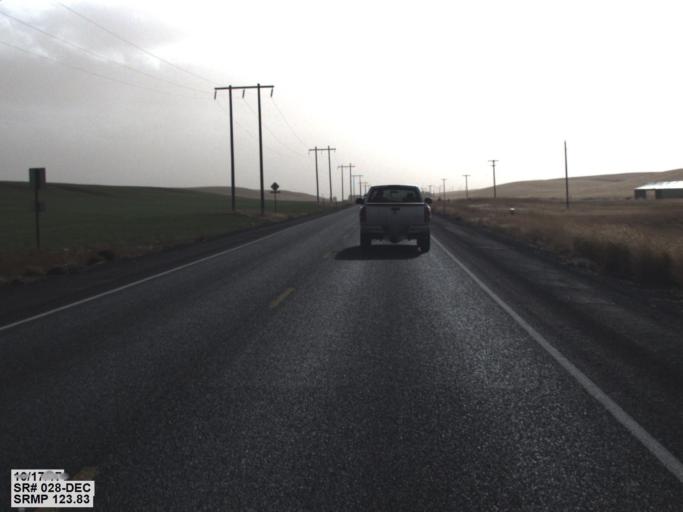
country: US
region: Washington
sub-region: Lincoln County
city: Davenport
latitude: 47.5522
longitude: -118.1835
